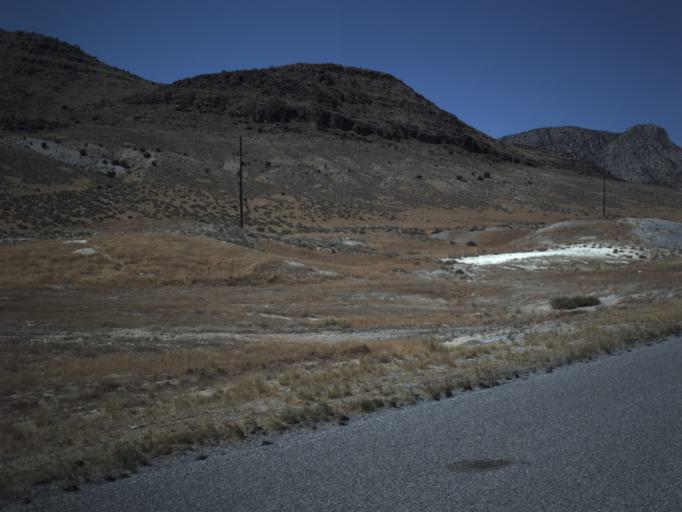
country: US
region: Utah
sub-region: Beaver County
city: Milford
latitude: 39.0851
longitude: -113.5167
